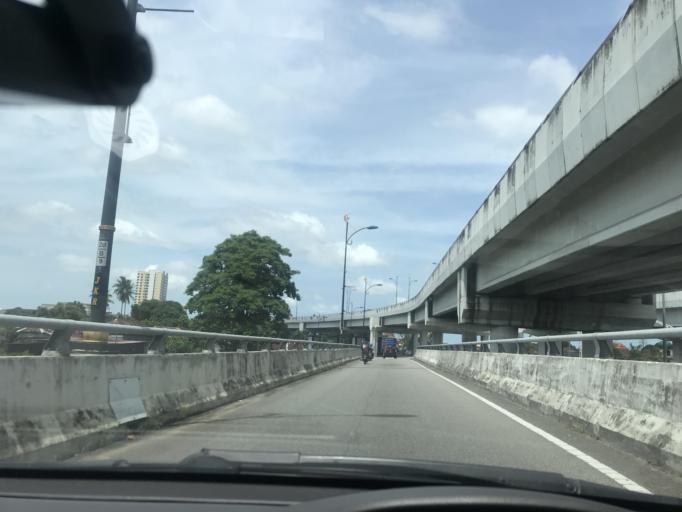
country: MY
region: Kelantan
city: Kota Bharu
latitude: 6.1158
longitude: 102.2336
